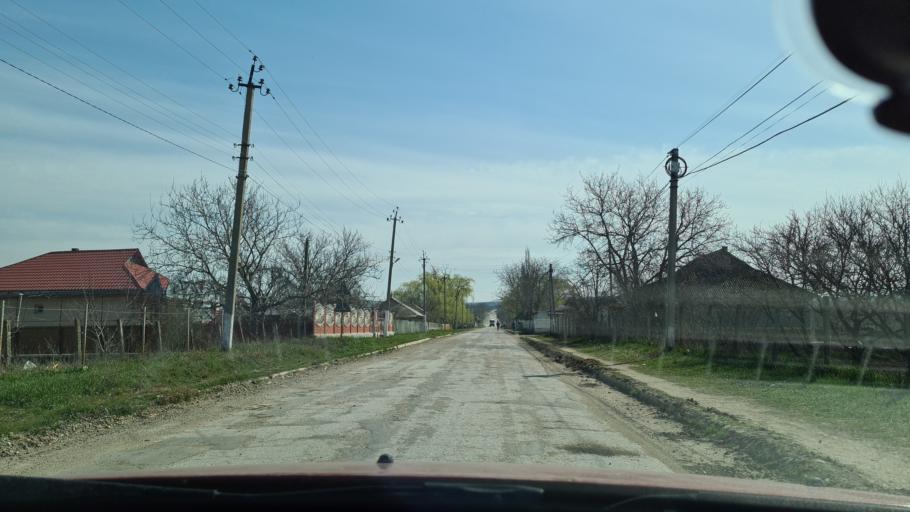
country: MD
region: Ungheni
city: Ungheni
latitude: 47.2690
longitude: 27.9330
